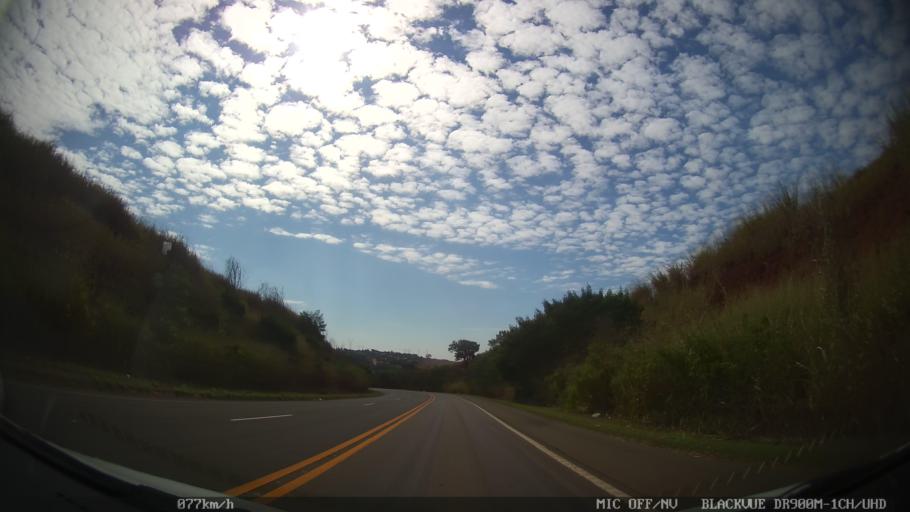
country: BR
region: Sao Paulo
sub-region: Santa Barbara D'Oeste
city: Santa Barbara d'Oeste
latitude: -22.7160
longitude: -47.4261
